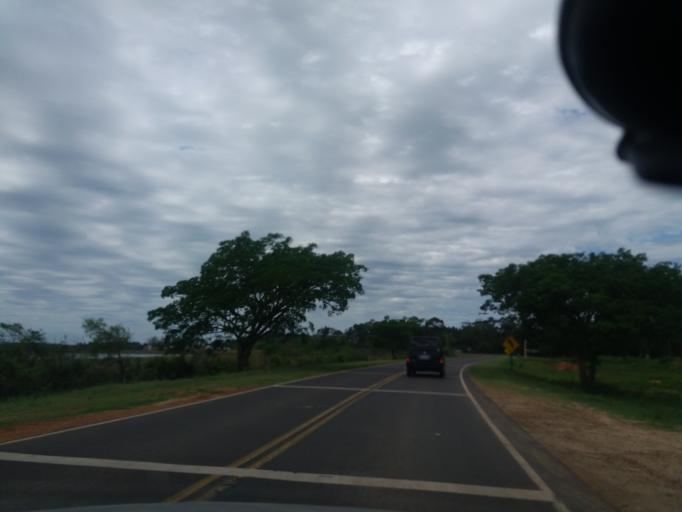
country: AR
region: Corrientes
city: Corrientes
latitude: -27.4535
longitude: -58.7218
